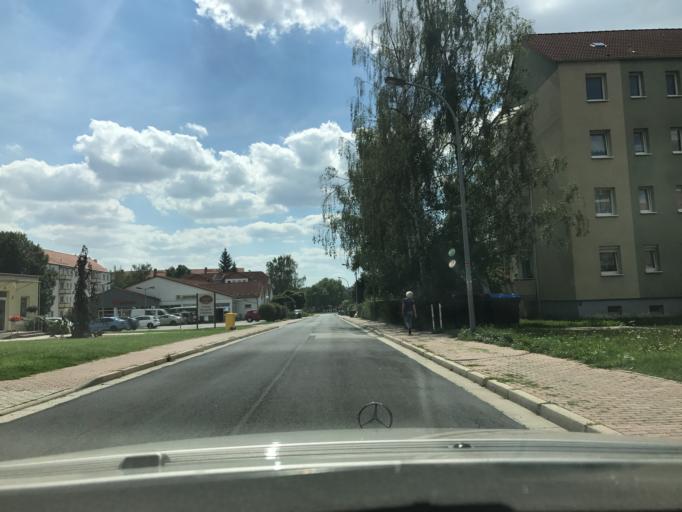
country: DE
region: Thuringia
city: Muehlhausen
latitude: 51.2176
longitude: 10.4730
